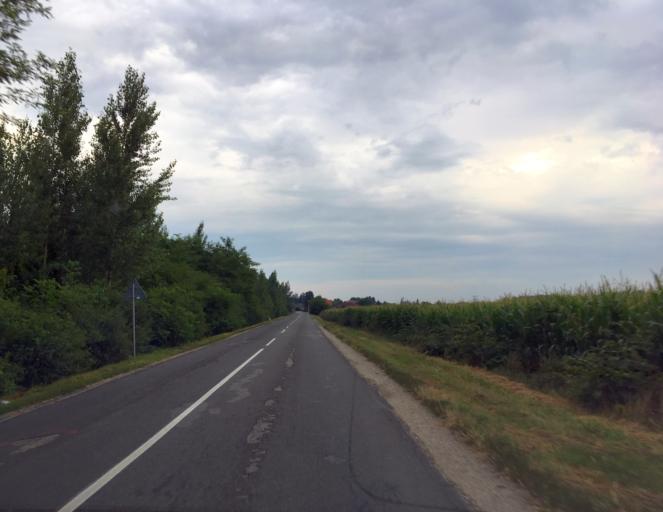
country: SK
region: Trnavsky
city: Gabcikovo
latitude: 47.8836
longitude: 17.6577
